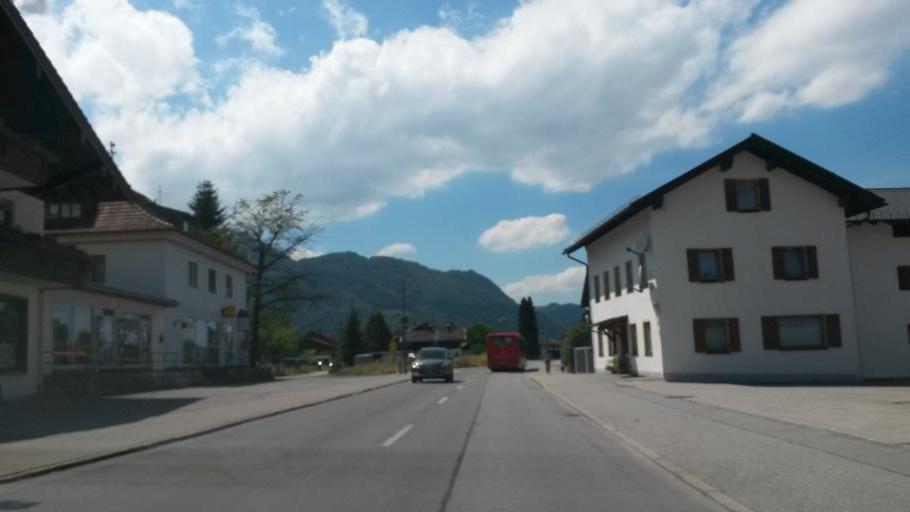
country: DE
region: Bavaria
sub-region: Upper Bavaria
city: Grassau
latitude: 47.7783
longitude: 12.4651
